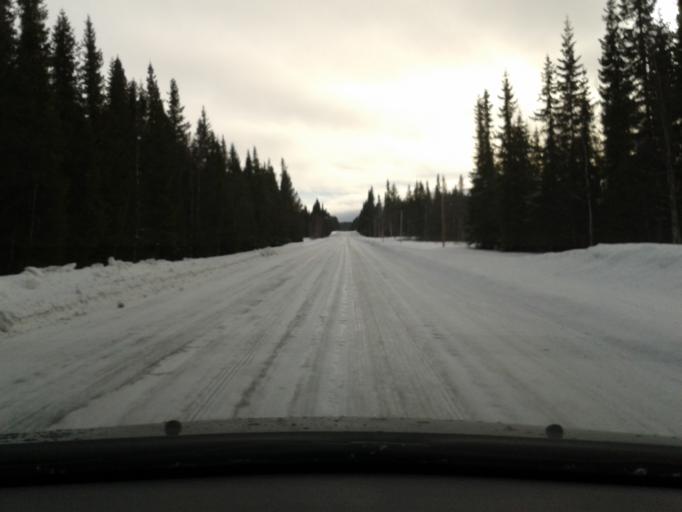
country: SE
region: Vaesterbotten
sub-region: Vilhelmina Kommun
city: Sjoberg
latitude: 64.7153
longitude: 16.2401
